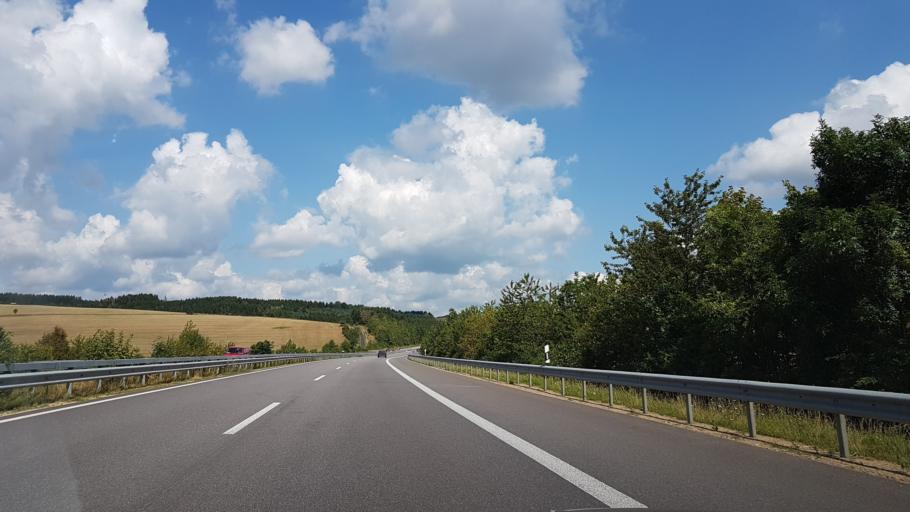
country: DE
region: Rheinland-Pfalz
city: Feuerscheid
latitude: 50.1057
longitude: 6.4414
